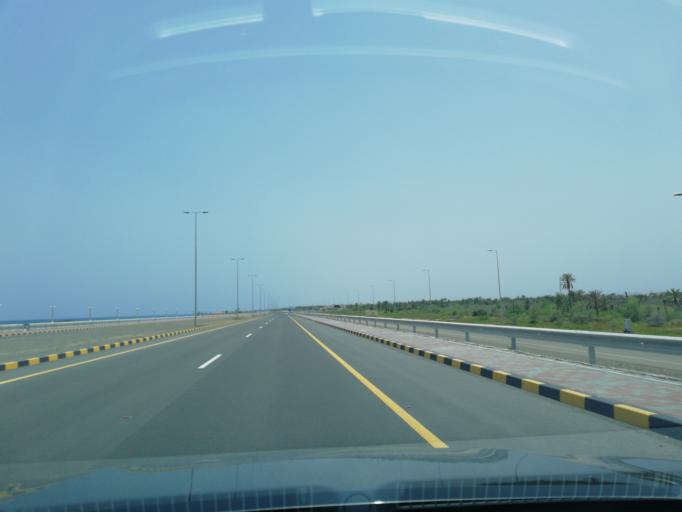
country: OM
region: Al Batinah
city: Shinas
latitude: 24.8220
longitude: 56.4395
